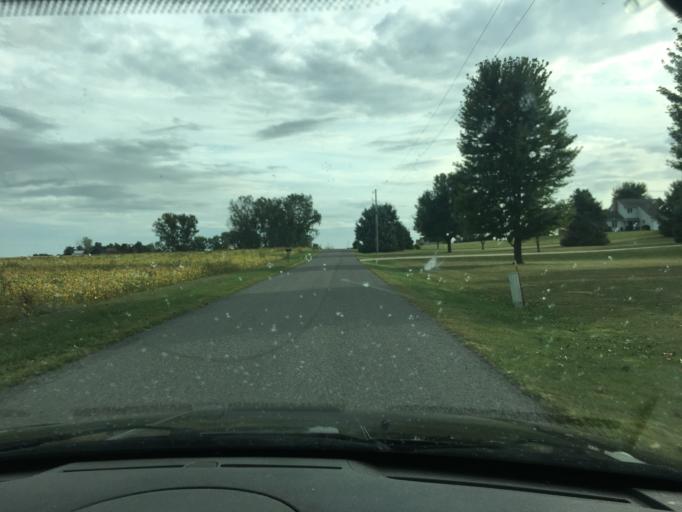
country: US
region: Ohio
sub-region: Logan County
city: Bellefontaine
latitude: 40.3258
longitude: -83.8057
